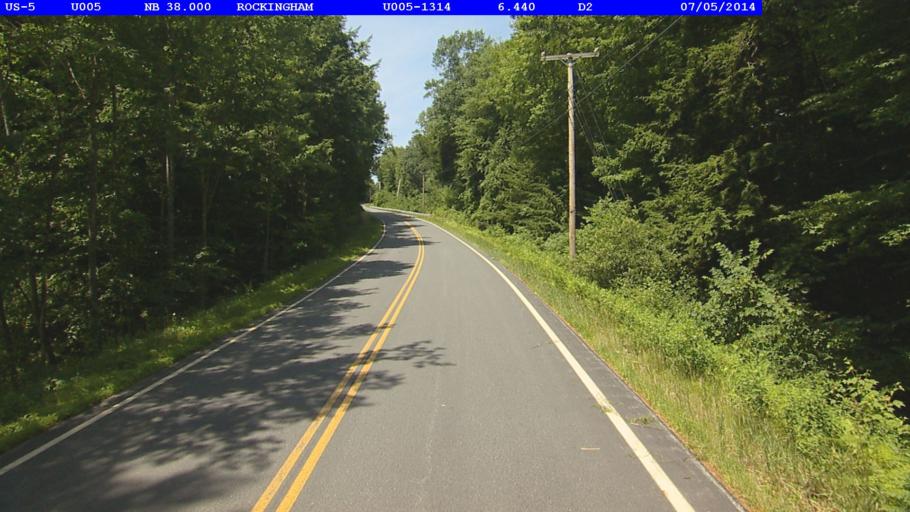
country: US
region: New Hampshire
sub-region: Sullivan County
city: Charlestown
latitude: 43.2076
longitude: -72.4494
